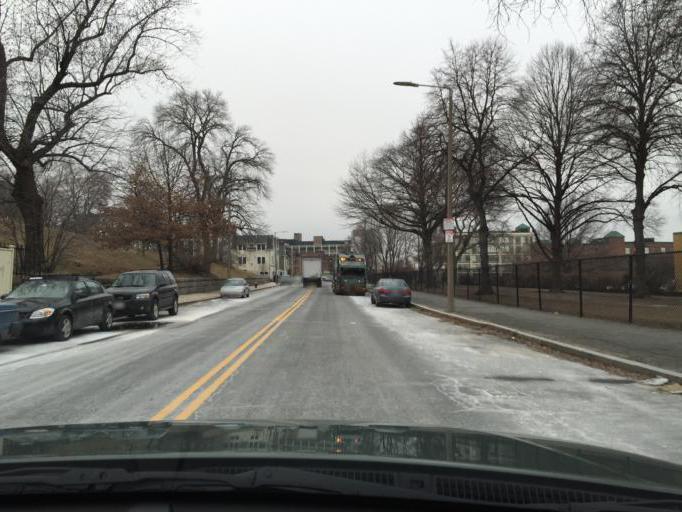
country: US
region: Massachusetts
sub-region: Suffolk County
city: Boston
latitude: 42.3827
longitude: -71.0662
